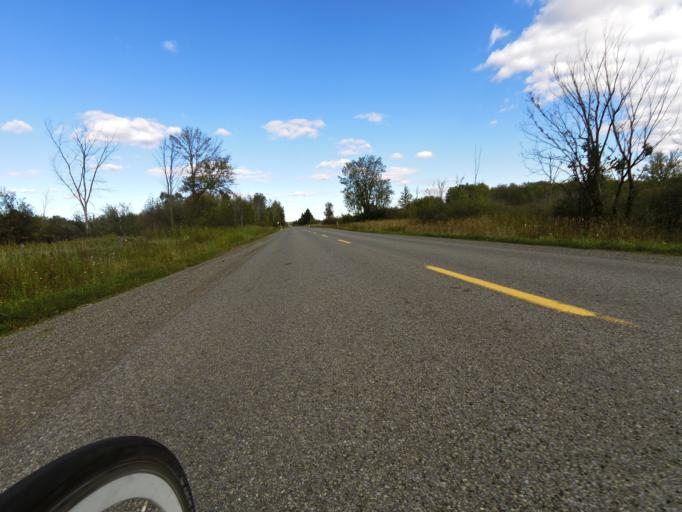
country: CA
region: Ontario
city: Bells Corners
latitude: 45.1002
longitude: -75.6381
